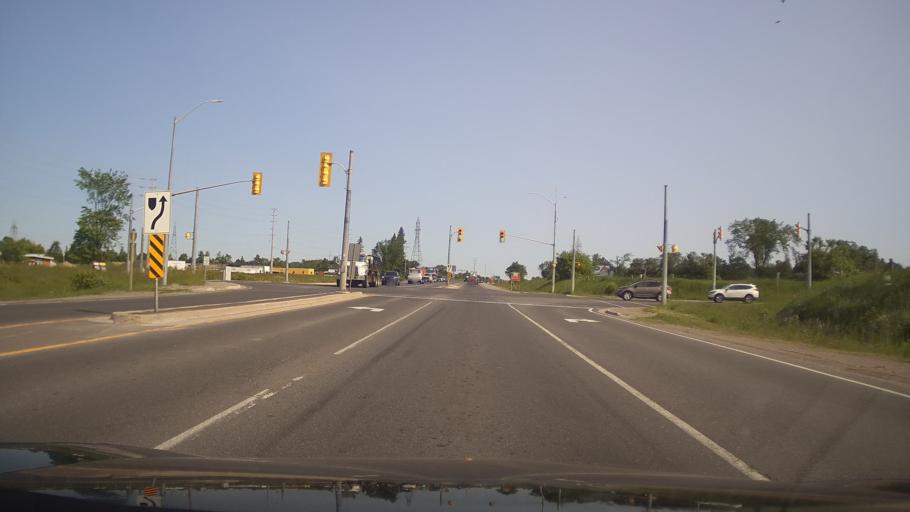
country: CA
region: Ontario
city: Peterborough
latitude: 44.2787
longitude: -78.4189
